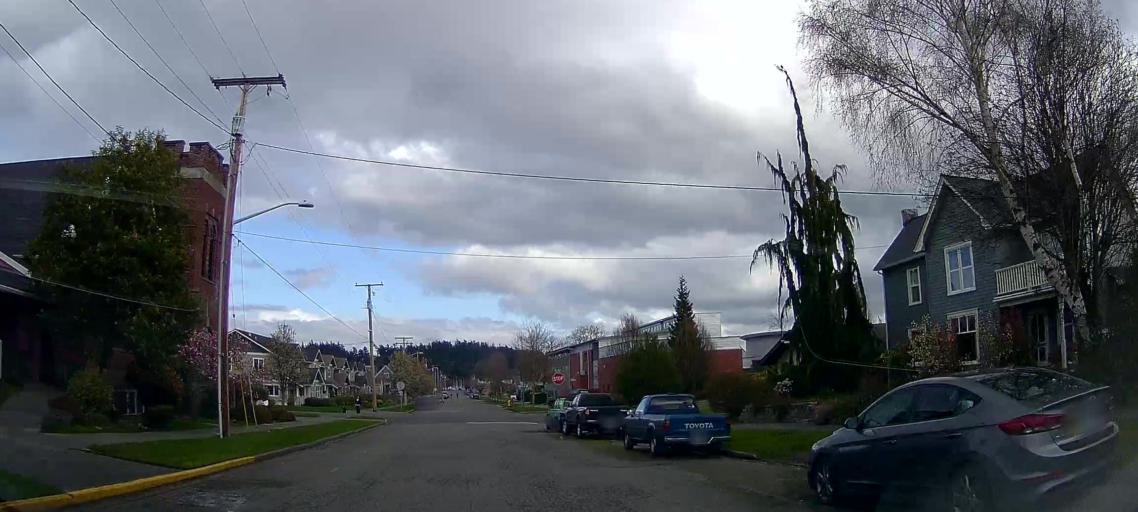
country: US
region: Washington
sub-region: Skagit County
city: Anacortes
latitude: 48.5151
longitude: -122.6180
